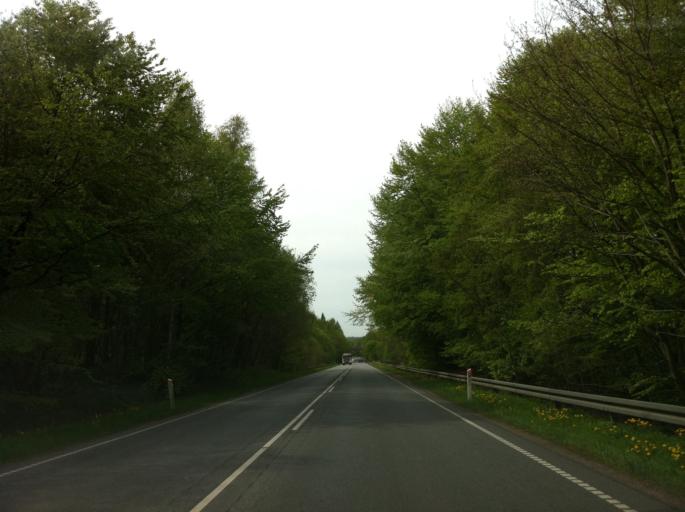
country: DK
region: Capital Region
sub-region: Hillerod Kommune
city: Hillerod
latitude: 55.9197
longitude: 12.3255
